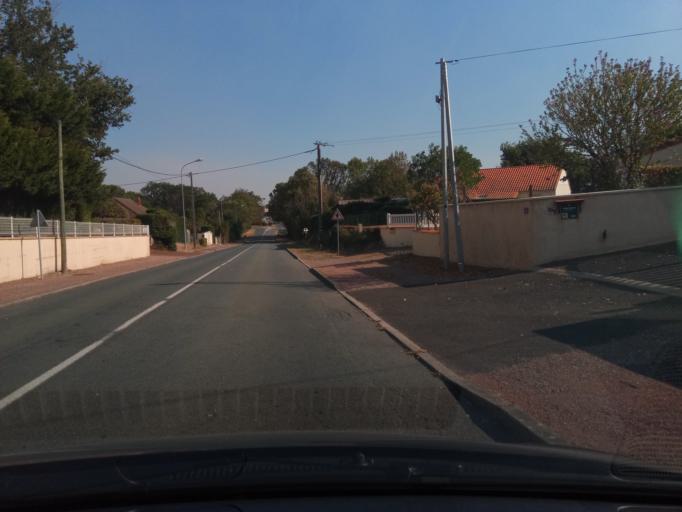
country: FR
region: Poitou-Charentes
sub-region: Departement de la Vienne
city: Montmorillon
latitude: 46.4279
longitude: 0.8562
